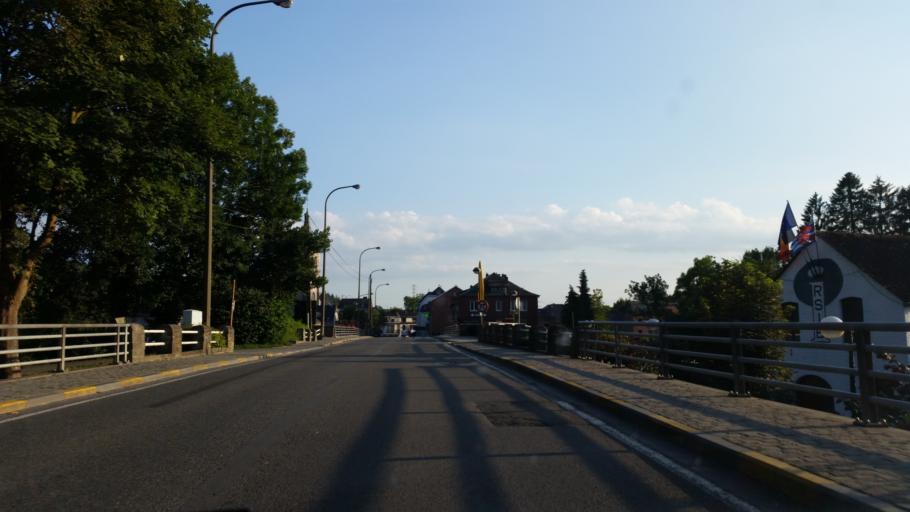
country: BE
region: Wallonia
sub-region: Province du Luxembourg
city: Durbuy
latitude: 50.3524
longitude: 5.4937
